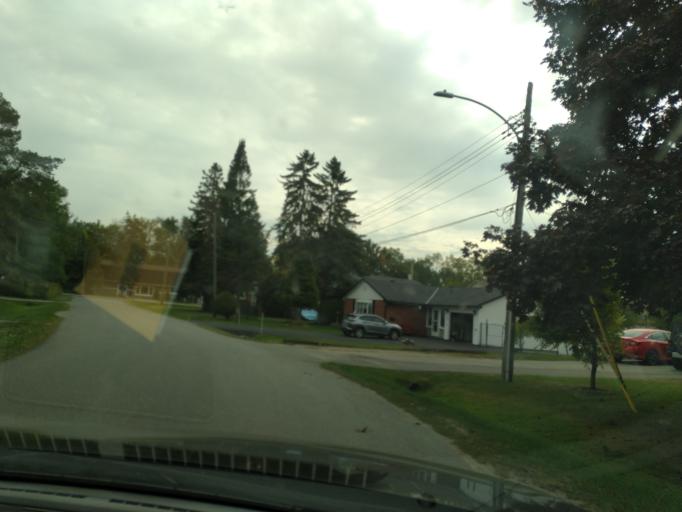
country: CA
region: Ontario
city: Keswick
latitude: 44.2459
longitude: -79.4768
